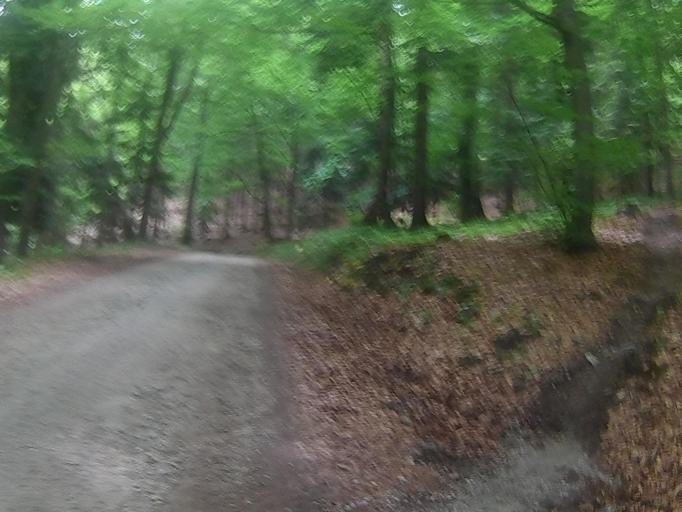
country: SI
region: Maribor
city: Pekre
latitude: 46.5237
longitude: 15.5806
